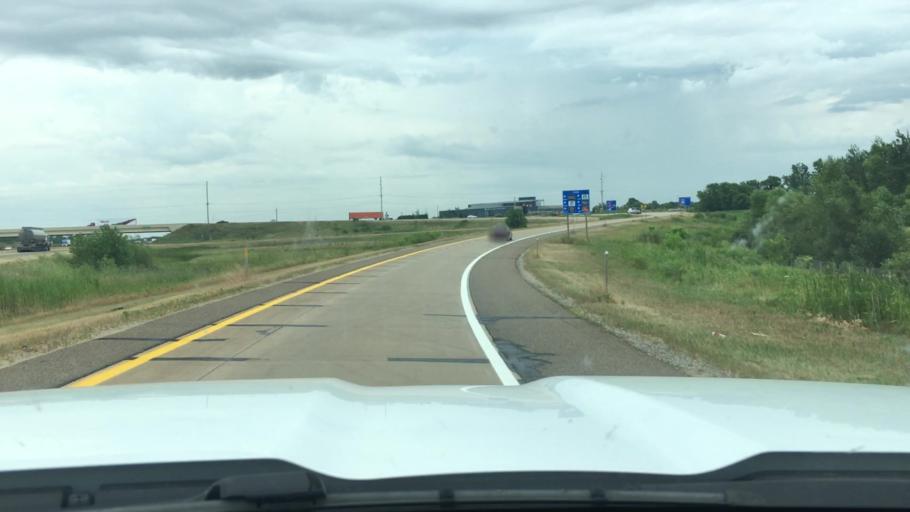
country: US
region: Michigan
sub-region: Kent County
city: Byron Center
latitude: 42.8525
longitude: -85.7282
